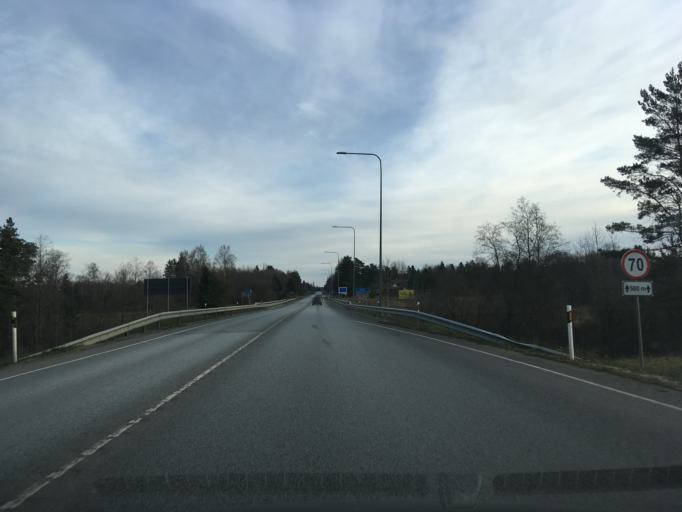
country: EE
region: Laeaene-Virumaa
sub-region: Viru-Nigula vald
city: Kunda
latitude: 59.3732
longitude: 26.5794
